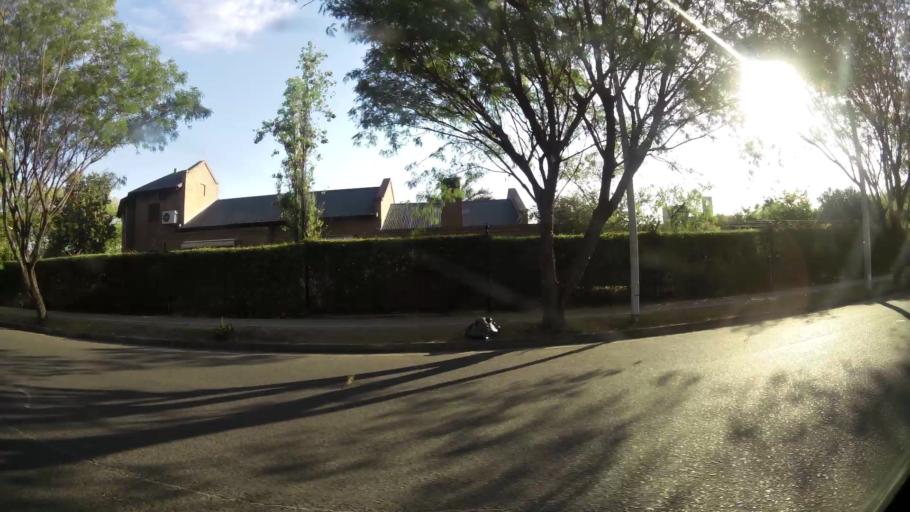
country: AR
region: Cordoba
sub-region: Departamento de Capital
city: Cordoba
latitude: -31.3790
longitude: -64.2453
